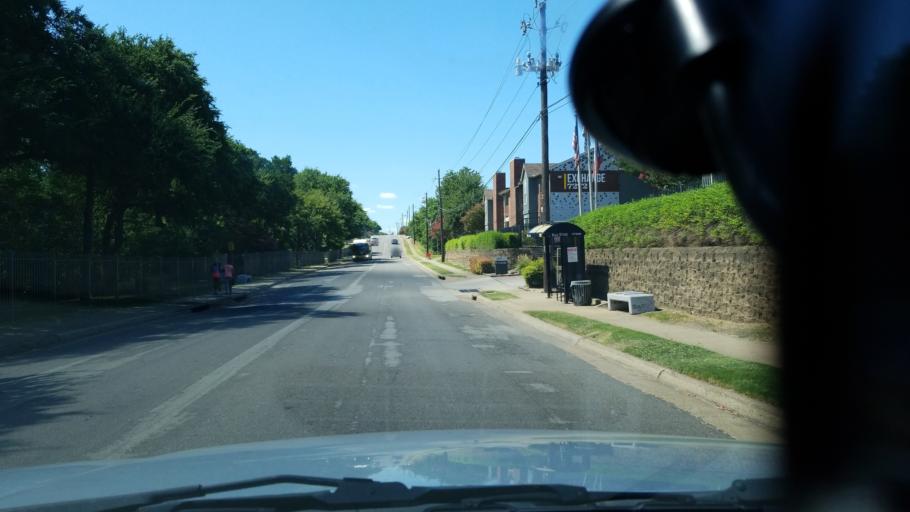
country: US
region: Texas
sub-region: Dallas County
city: Duncanville
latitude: 32.6592
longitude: -96.8699
